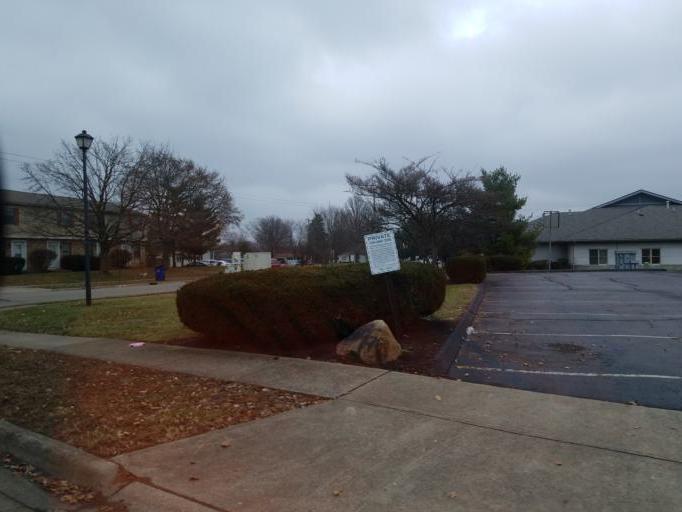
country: US
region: Ohio
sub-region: Franklin County
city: Minerva Park
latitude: 40.0935
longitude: -82.9521
